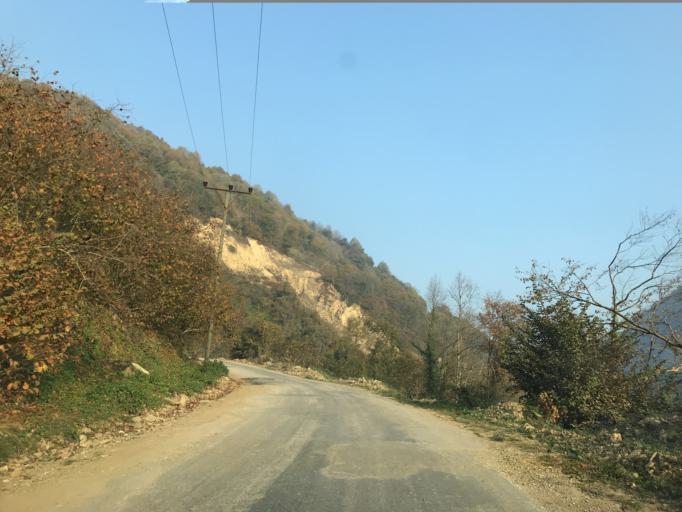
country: TR
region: Duzce
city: Cumayeri
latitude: 40.9206
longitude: 30.9292
